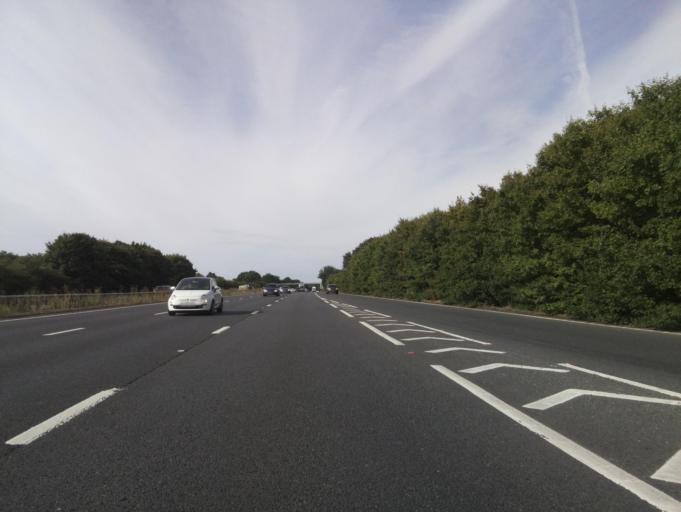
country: GB
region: England
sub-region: Surrey
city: Ripley
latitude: 51.2919
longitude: -0.4905
